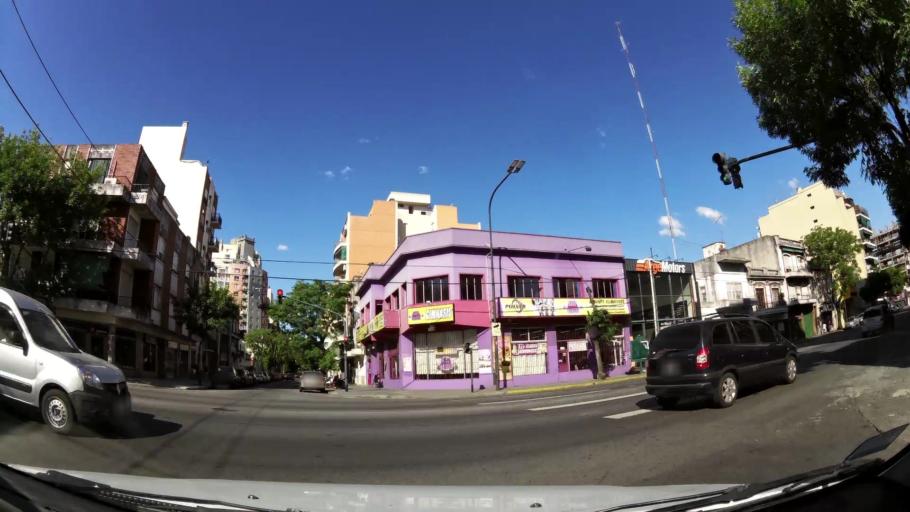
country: AR
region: Buenos Aires F.D.
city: Villa Santa Rita
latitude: -34.6164
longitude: -58.4775
